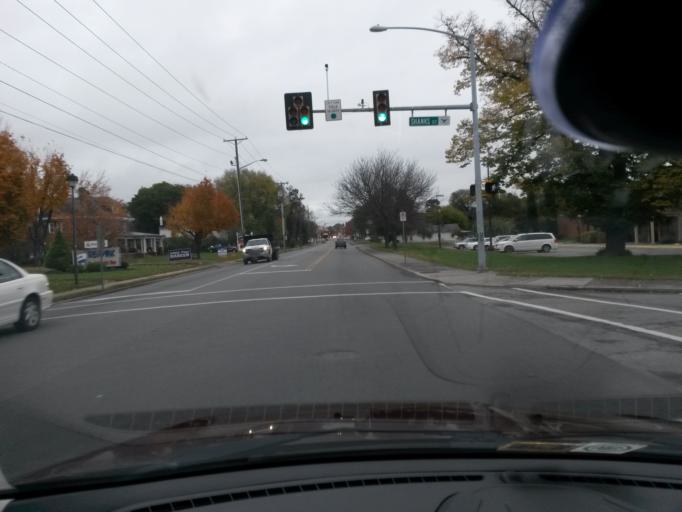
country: US
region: Virginia
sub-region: City of Salem
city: Salem
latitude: 37.2914
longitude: -80.0655
